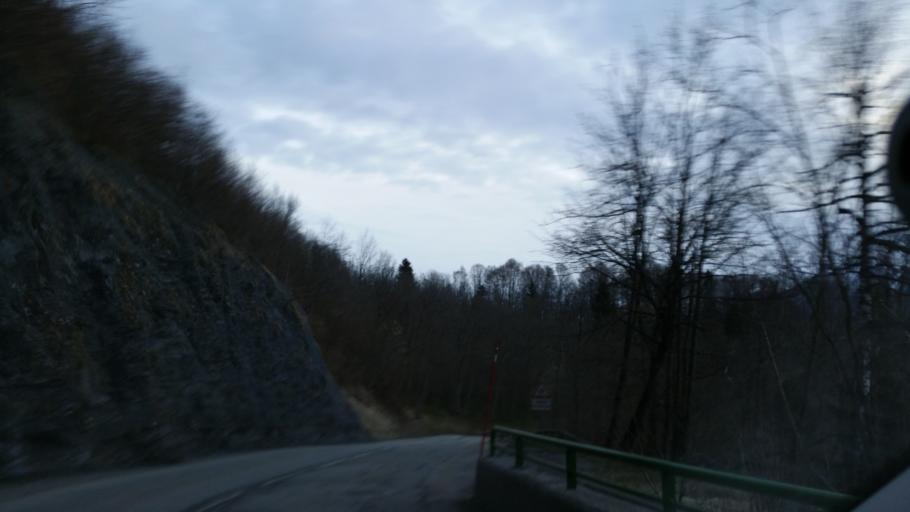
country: FR
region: Rhone-Alpes
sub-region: Departement de la Savoie
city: La Chambre
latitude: 45.3885
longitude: 6.3371
